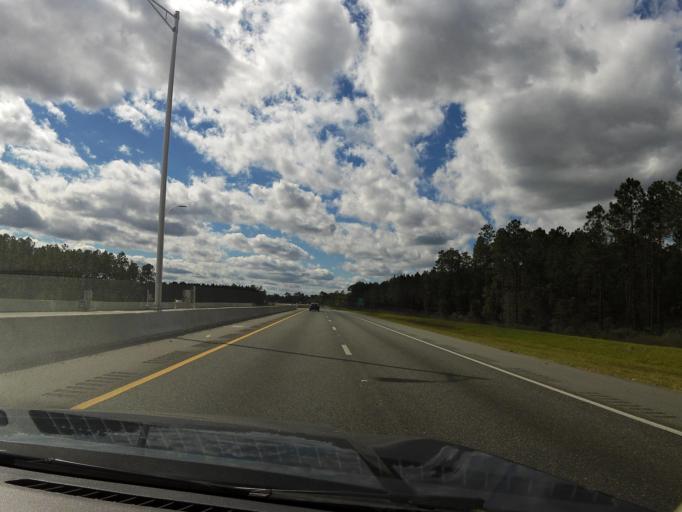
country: US
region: Florida
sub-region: Bradford County
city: Starke
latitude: 29.9878
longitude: -82.1057
